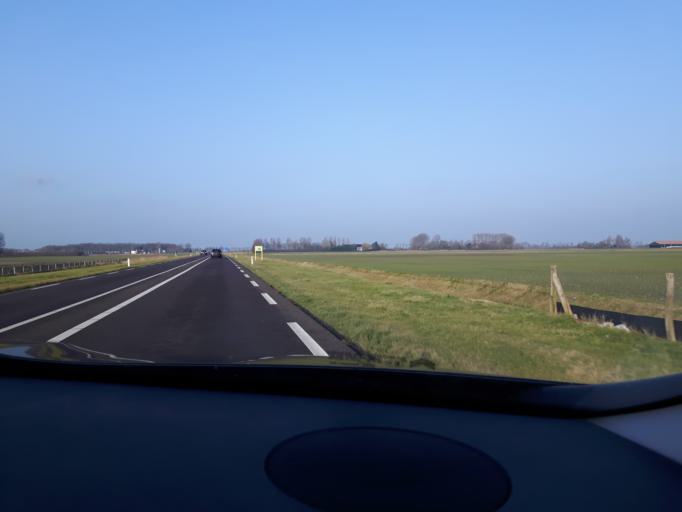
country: NL
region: Zeeland
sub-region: Gemeente Middelburg
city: Middelburg
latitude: 51.5358
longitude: 3.6094
